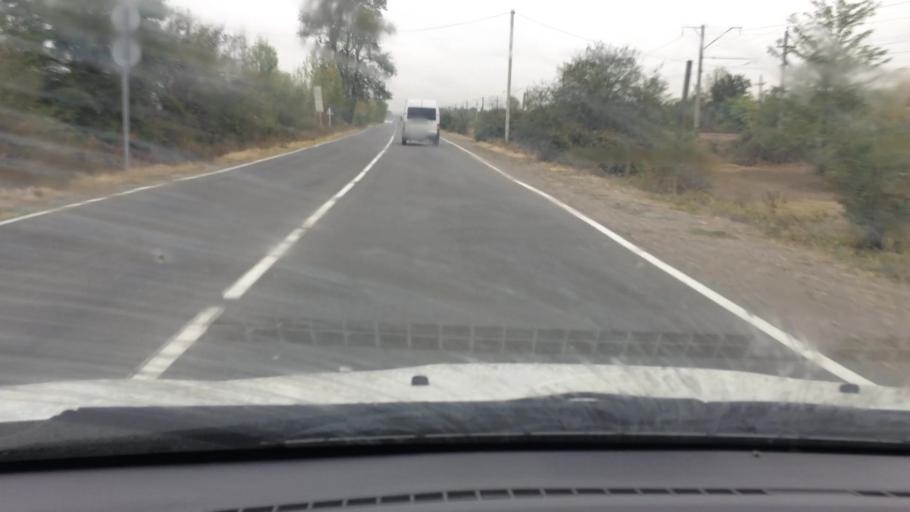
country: GE
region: Kvemo Kartli
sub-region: Marneuli
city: Marneuli
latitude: 41.4413
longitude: 44.8172
